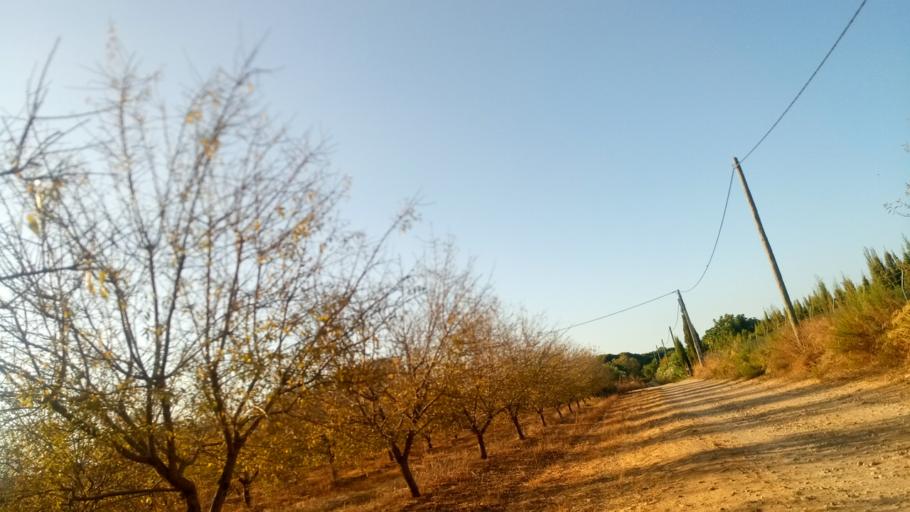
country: PT
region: Faro
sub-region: Tavira
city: Tavira
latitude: 37.1454
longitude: -7.5832
